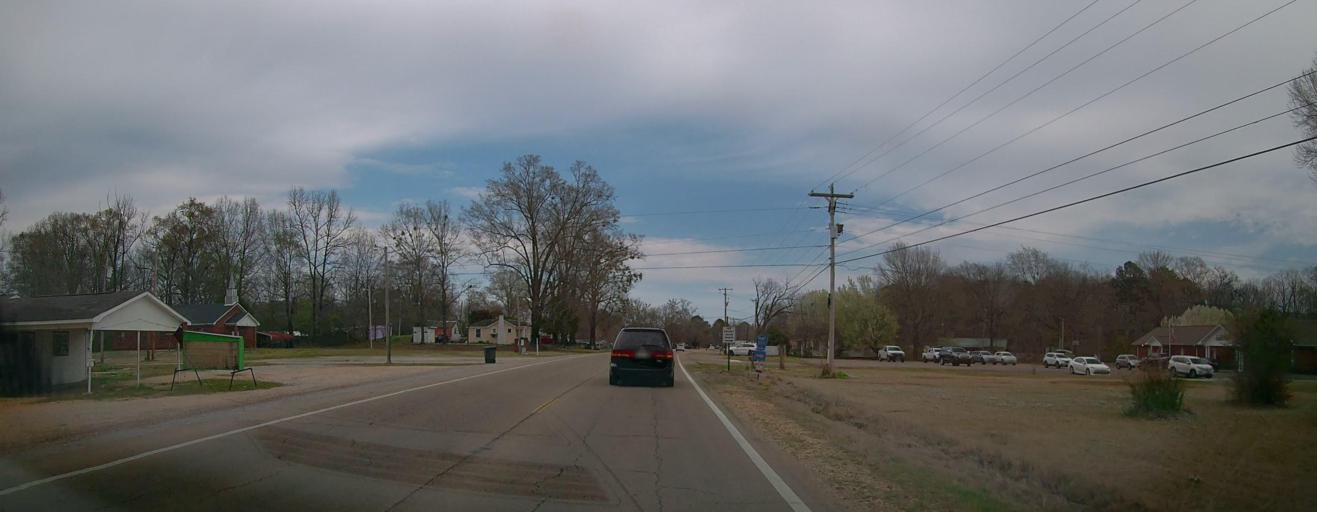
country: US
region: Mississippi
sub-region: Lee County
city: Plantersville
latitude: 34.2630
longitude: -88.6433
